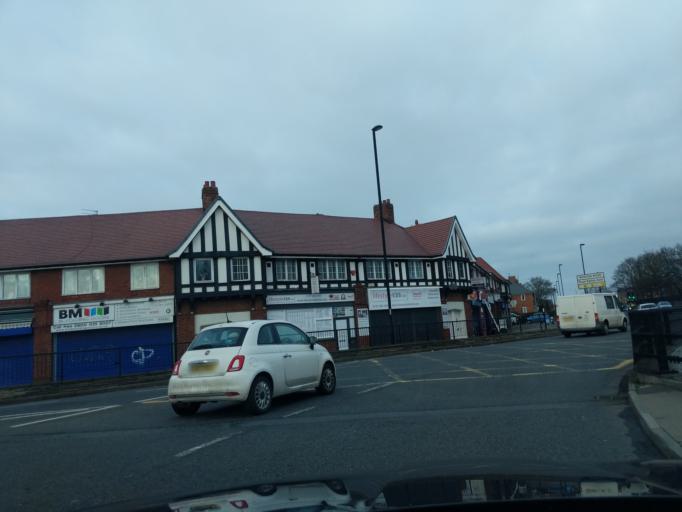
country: GB
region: England
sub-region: Gateshead
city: Gateshead
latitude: 54.9926
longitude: -1.5795
